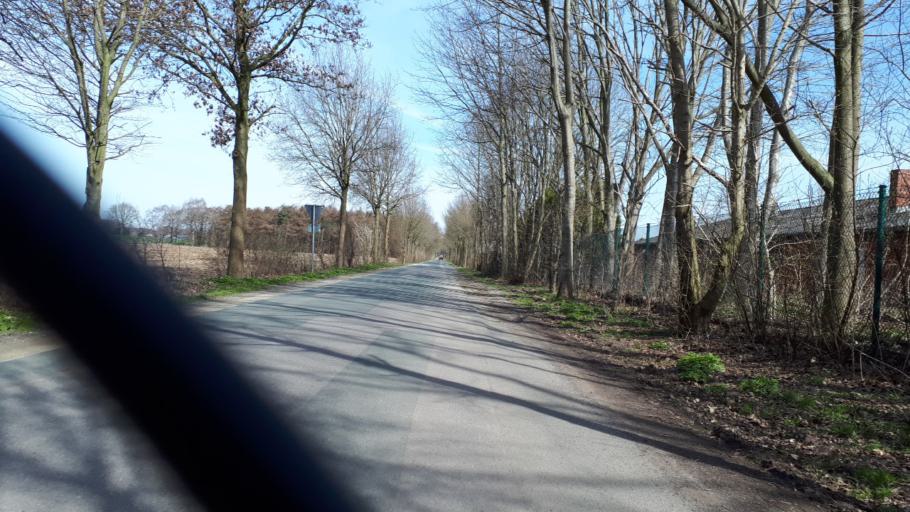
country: DE
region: Lower Saxony
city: Cloppenburg
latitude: 52.8595
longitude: 7.9939
